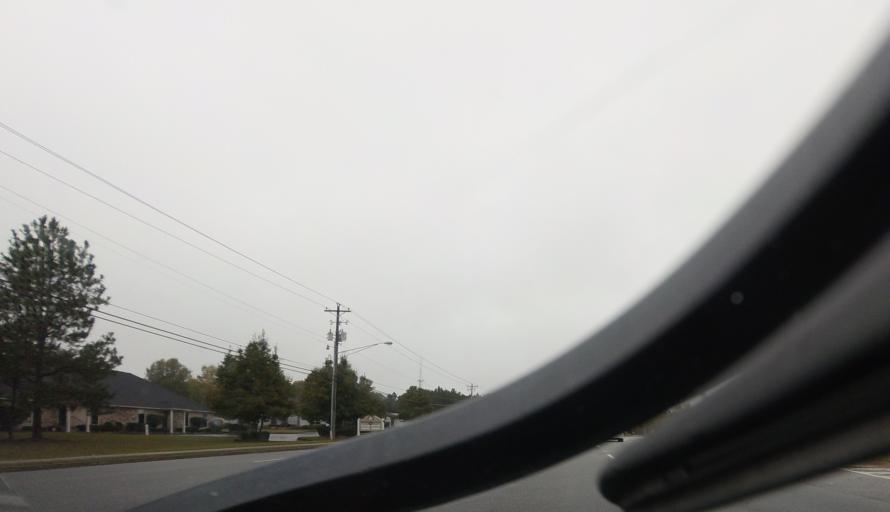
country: US
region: Georgia
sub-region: Houston County
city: Centerville
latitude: 32.5972
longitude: -83.6651
